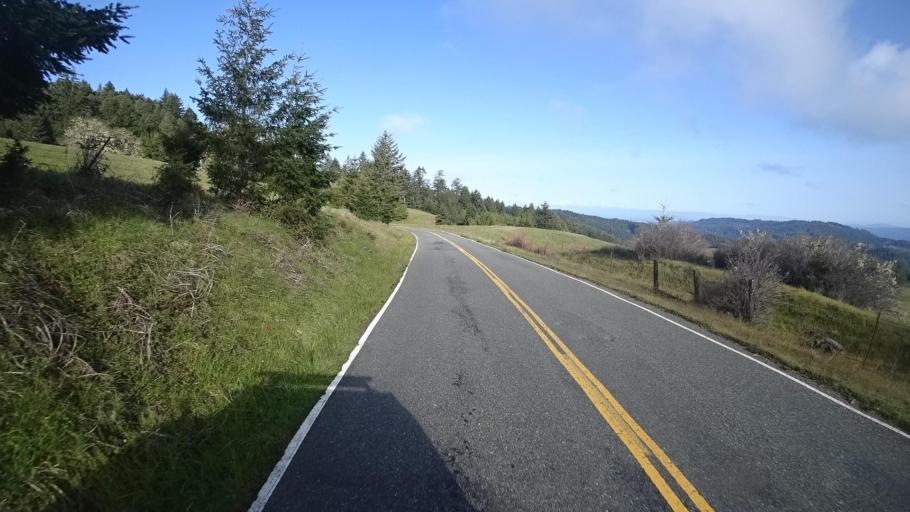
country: US
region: California
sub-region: Humboldt County
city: Blue Lake
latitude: 40.7377
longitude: -123.9476
